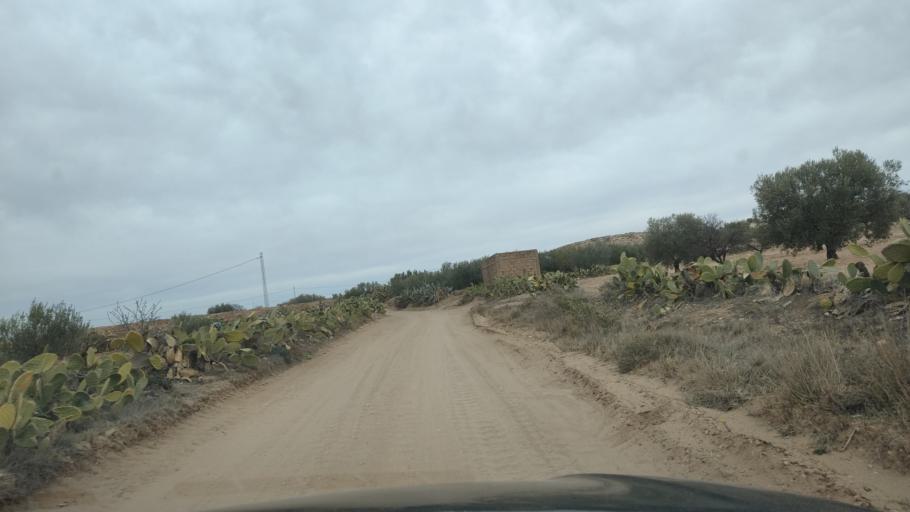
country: TN
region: Al Qasrayn
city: Kasserine
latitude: 35.2451
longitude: 8.9184
